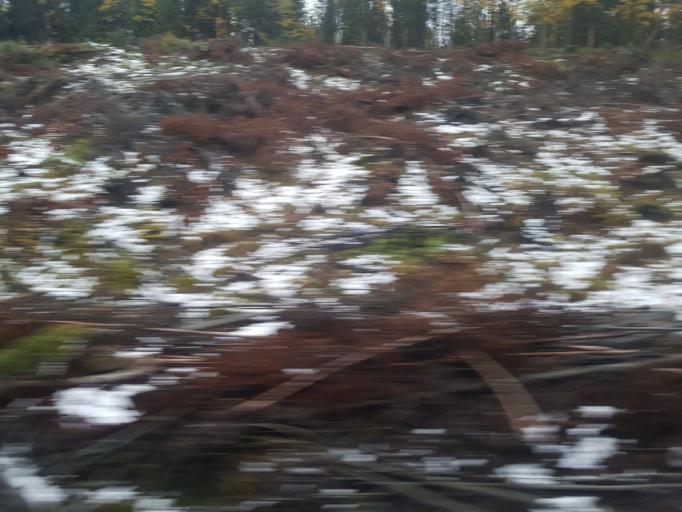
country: NO
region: Sor-Trondelag
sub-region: Rennebu
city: Berkak
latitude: 62.7148
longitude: 10.0310
